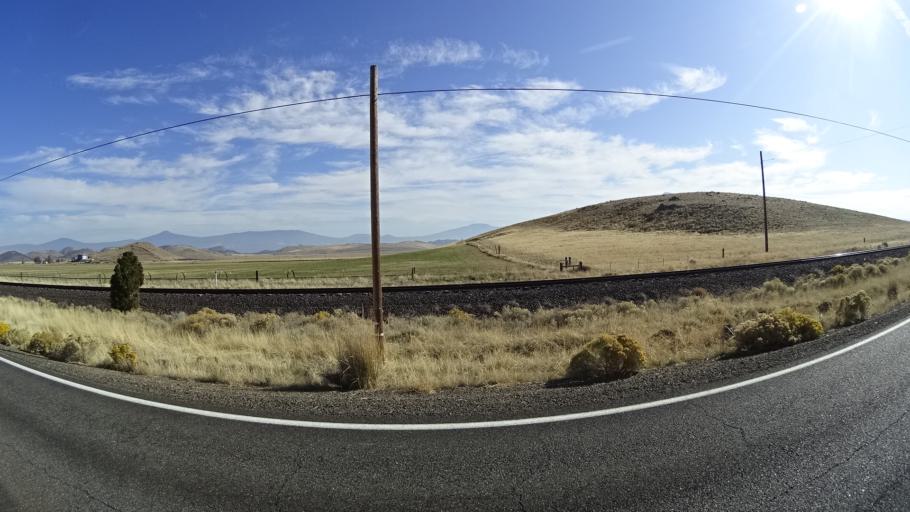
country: US
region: California
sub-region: Siskiyou County
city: Montague
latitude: 41.5552
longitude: -122.5267
